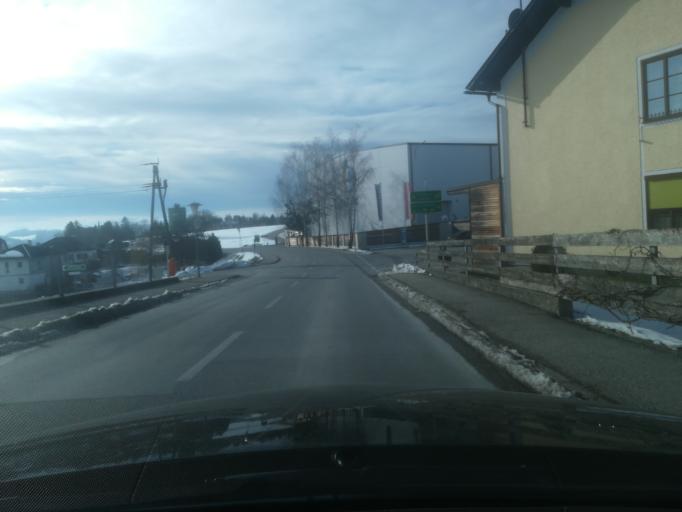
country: AT
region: Upper Austria
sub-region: Politischer Bezirk Perg
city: Perg
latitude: 48.3273
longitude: 14.6231
